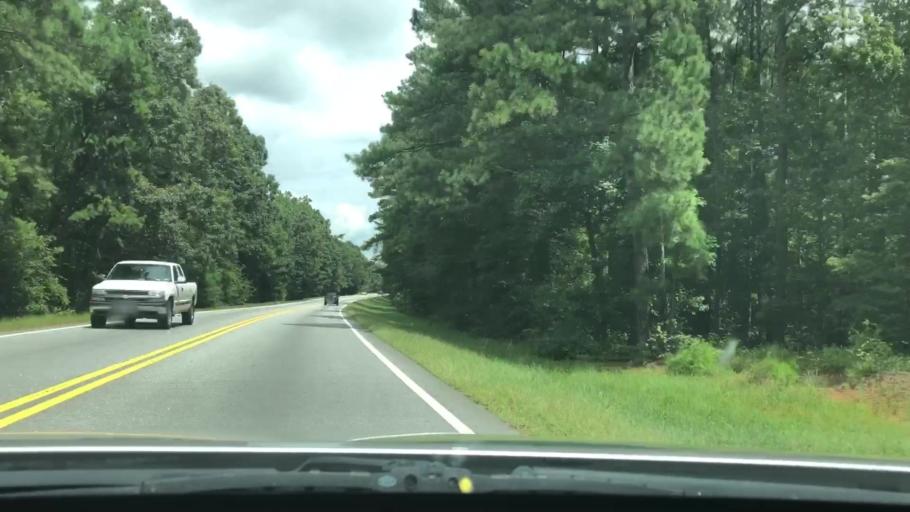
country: US
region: Georgia
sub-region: Lamar County
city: Barnesville
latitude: 33.1634
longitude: -84.1046
